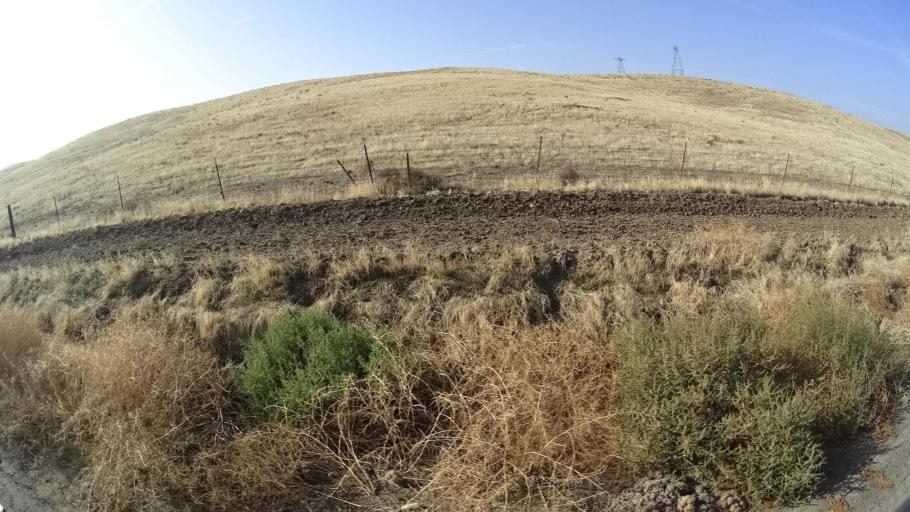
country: US
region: California
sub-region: Tulare County
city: Richgrove
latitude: 35.6374
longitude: -119.0392
